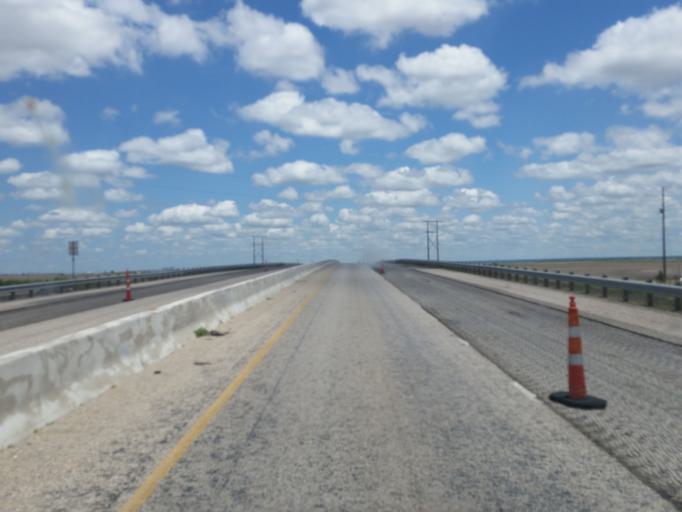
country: US
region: Texas
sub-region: Nolan County
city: Roscoe
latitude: 32.4508
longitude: -100.5223
